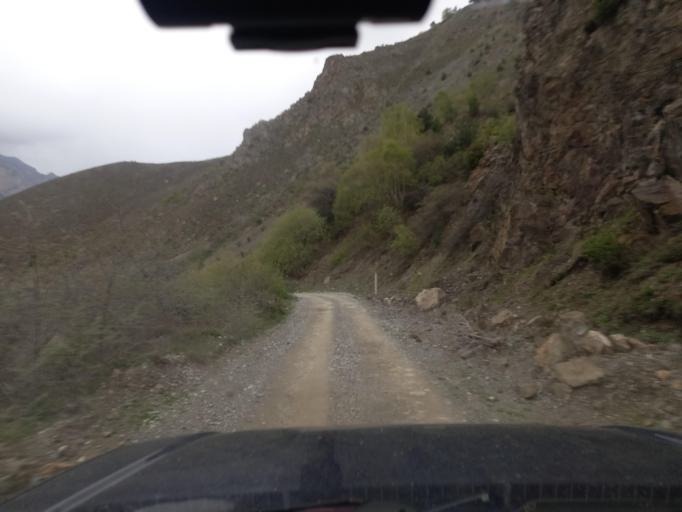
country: RU
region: North Ossetia
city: Mizur
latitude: 42.8528
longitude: 44.1618
